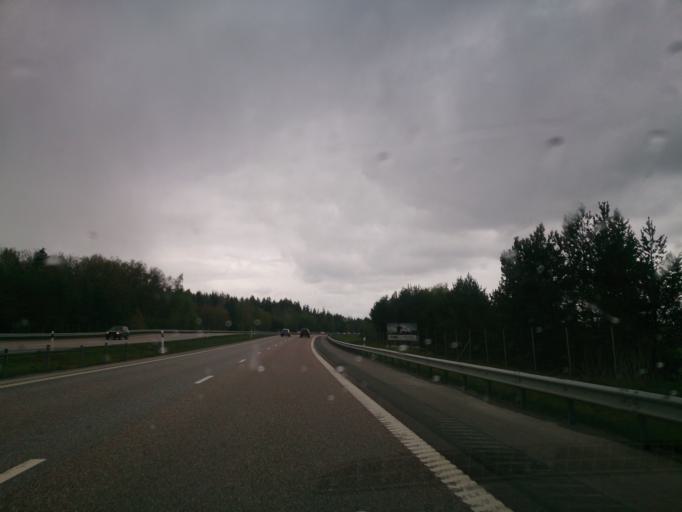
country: SE
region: Soedermanland
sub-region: Trosa Kommun
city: Vagnharad
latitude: 59.0479
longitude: 17.5666
